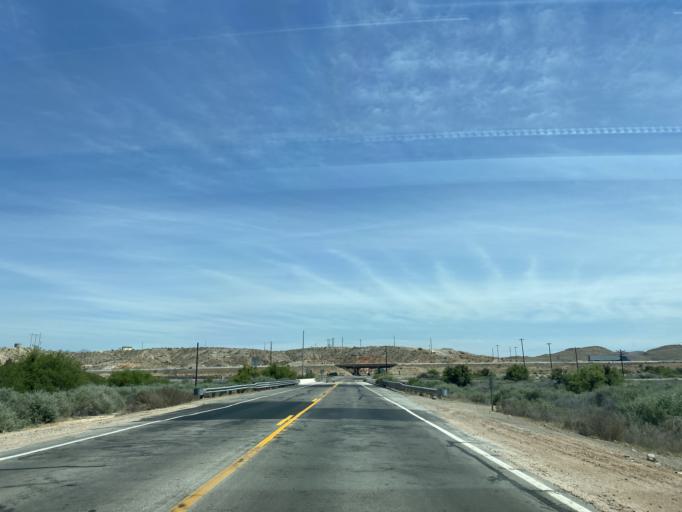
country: US
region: Nevada
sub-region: Clark County
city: Moapa Town
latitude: 36.6625
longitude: -114.5773
